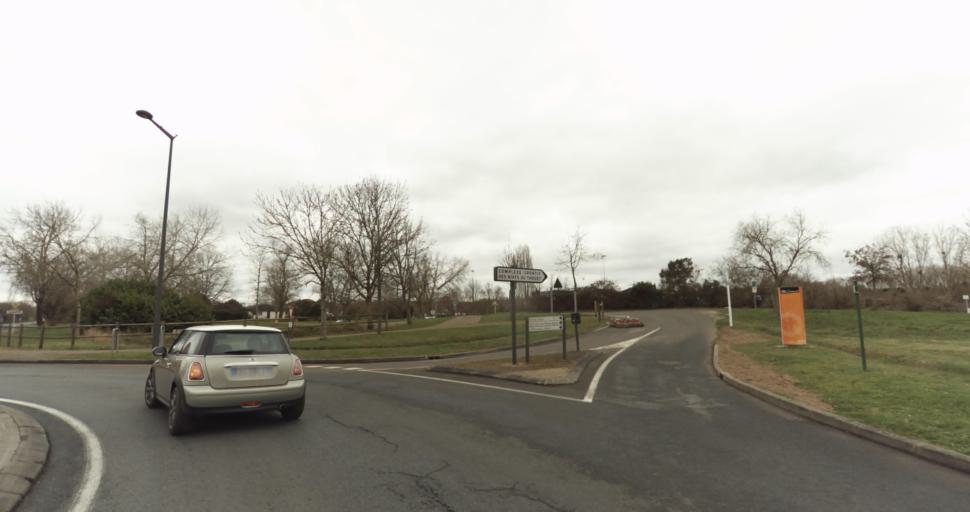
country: FR
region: Pays de la Loire
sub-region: Departement de Maine-et-Loire
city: Saumur
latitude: 47.2471
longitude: -0.0793
